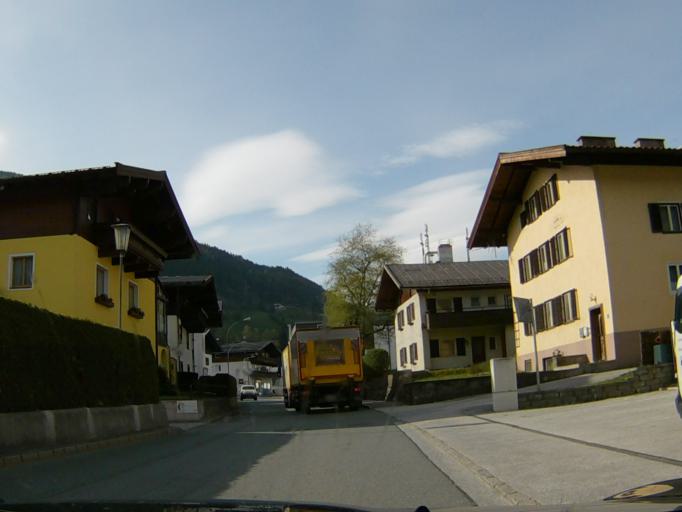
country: AT
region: Salzburg
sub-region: Politischer Bezirk Zell am See
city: Mittersill
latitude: 47.2779
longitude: 12.4842
